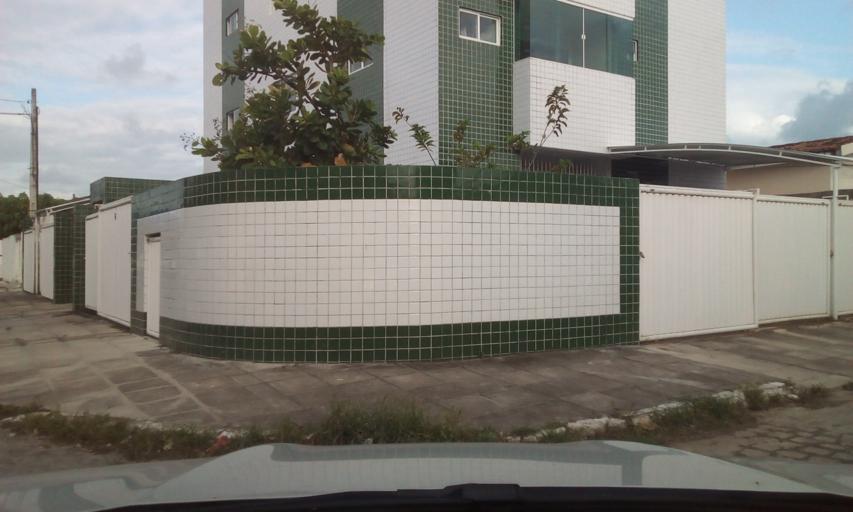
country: BR
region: Paraiba
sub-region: Joao Pessoa
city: Joao Pessoa
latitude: -7.1627
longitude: -34.8403
